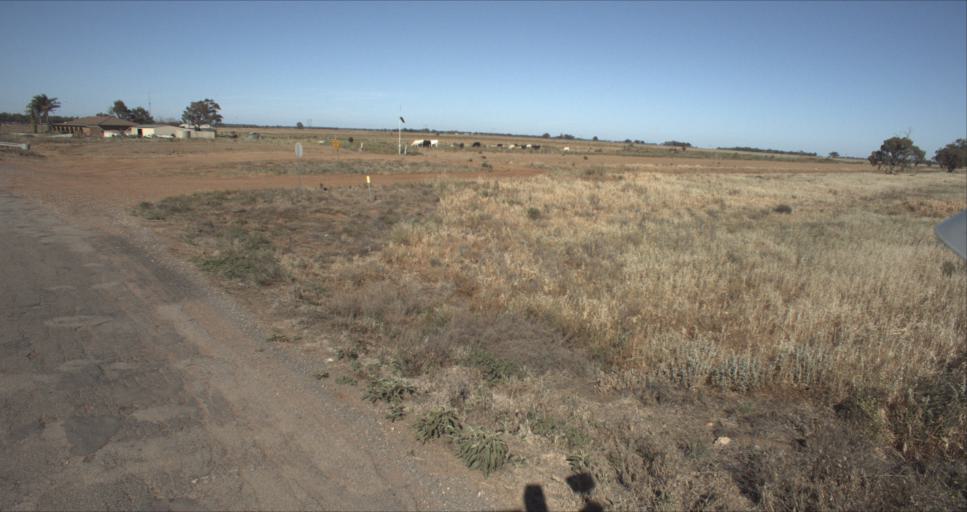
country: AU
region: New South Wales
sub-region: Leeton
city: Leeton
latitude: -34.5672
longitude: 146.3115
